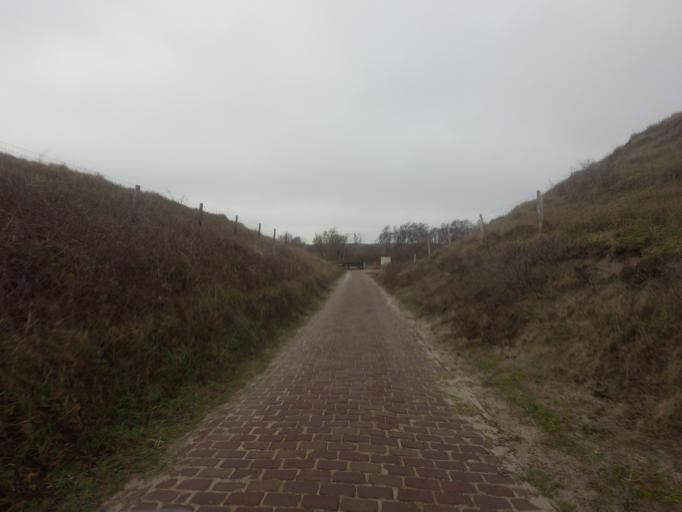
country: NL
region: North Holland
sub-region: Gemeente Texel
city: Den Burg
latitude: 53.1203
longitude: 4.8012
